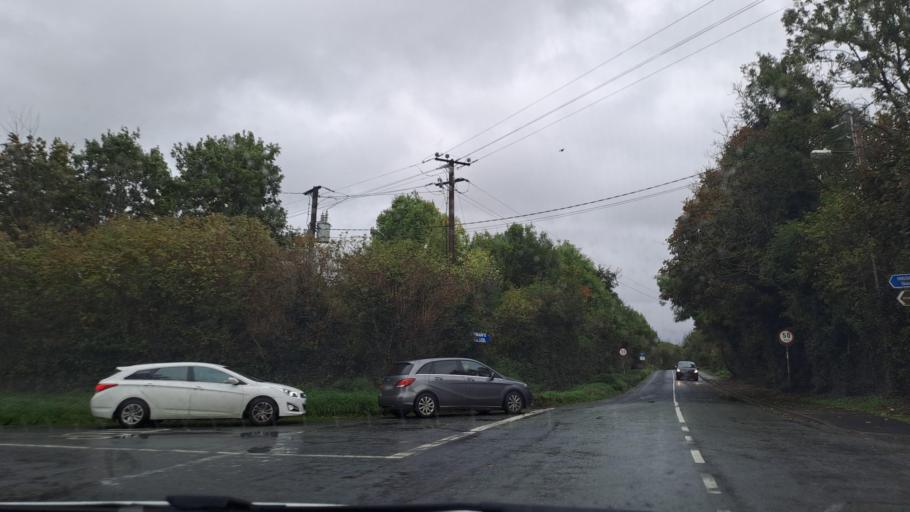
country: IE
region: Leinster
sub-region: Lu
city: Dromiskin
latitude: 53.9636
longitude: -6.4136
